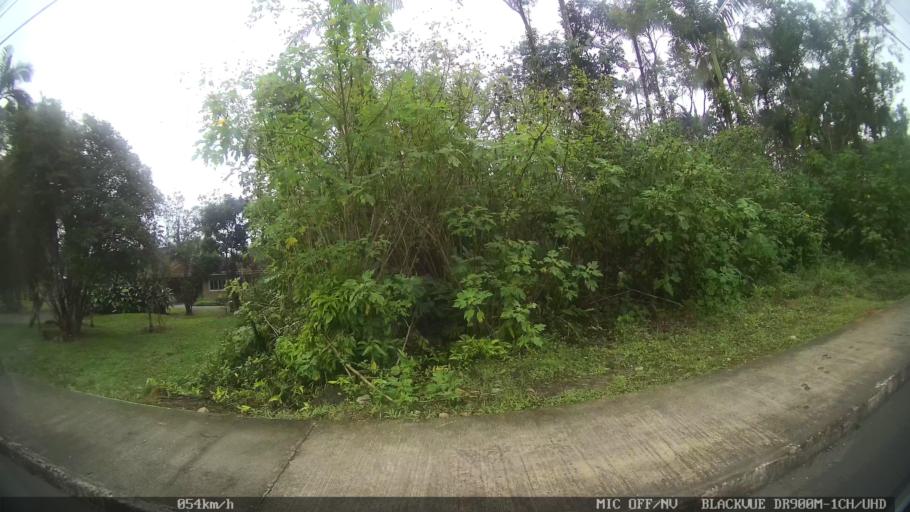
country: BR
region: Santa Catarina
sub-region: Joinville
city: Joinville
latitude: -26.0636
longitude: -48.8571
